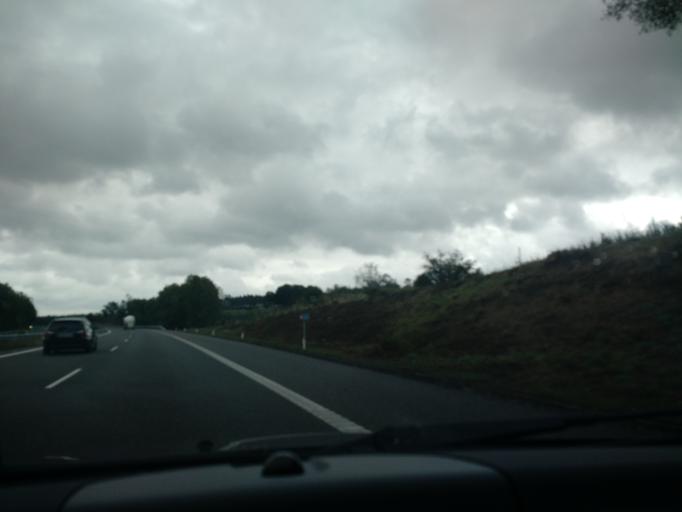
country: ES
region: Galicia
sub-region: Provincia da Coruna
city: Ordes
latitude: 43.0368
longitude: -8.3913
